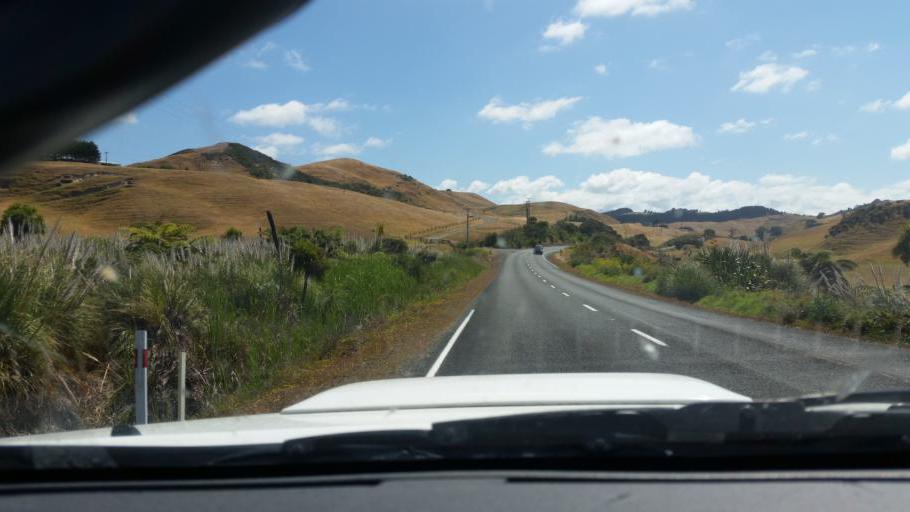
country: NZ
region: Northland
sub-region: Kaipara District
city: Dargaville
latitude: -35.8307
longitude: 173.6676
